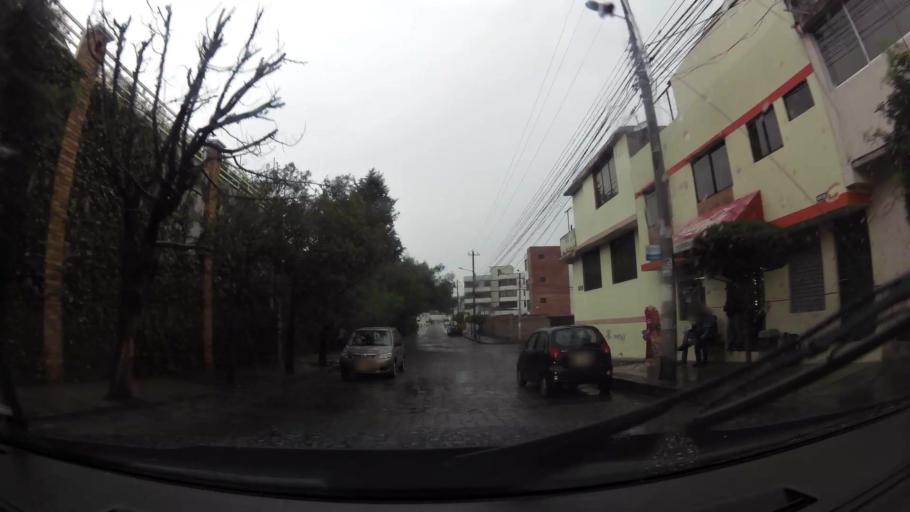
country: EC
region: Pichincha
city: Quito
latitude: -0.1581
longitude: -78.4609
